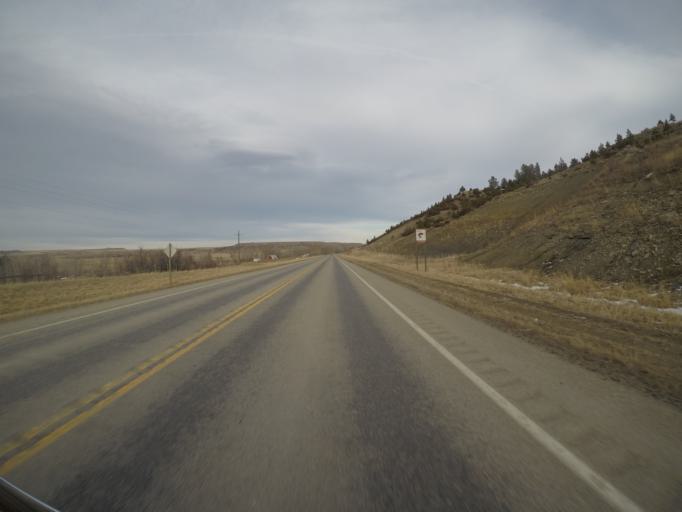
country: US
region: Montana
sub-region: Stillwater County
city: Absarokee
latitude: 45.5338
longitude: -109.4242
